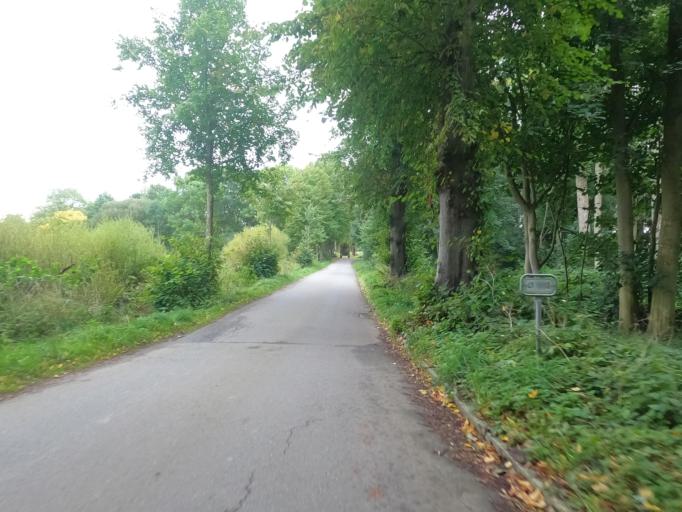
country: DE
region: Schleswig-Holstein
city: Neukirchen
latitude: 54.2896
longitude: 11.0584
